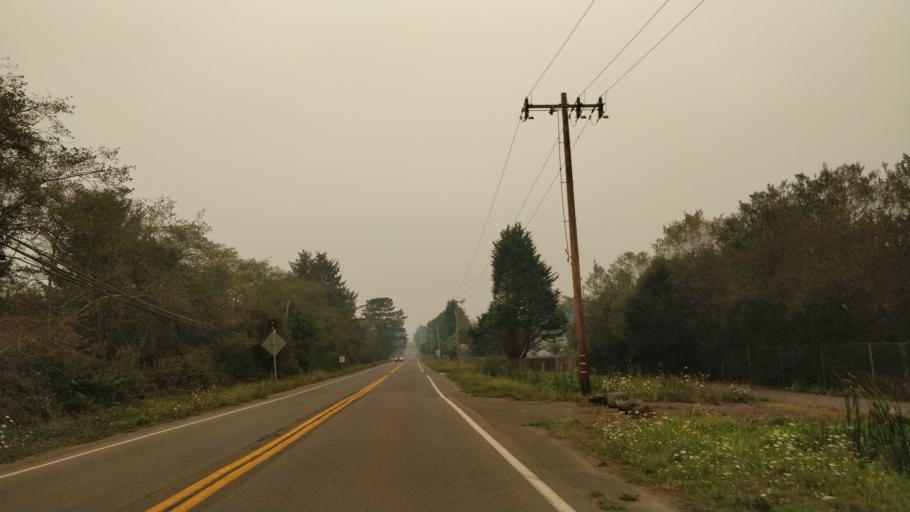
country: US
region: California
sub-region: Humboldt County
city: McKinleyville
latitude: 40.9572
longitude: -124.1008
